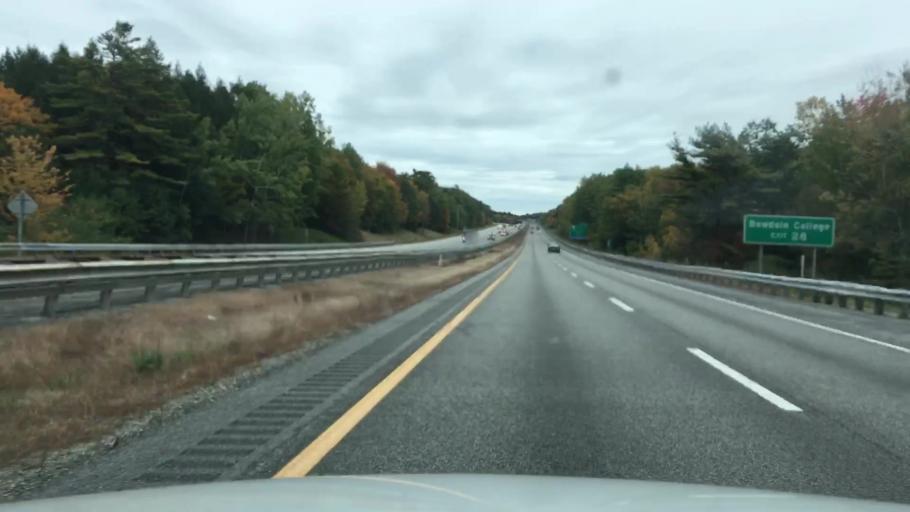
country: US
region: Maine
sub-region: Sagadahoc County
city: Topsham
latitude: 43.9094
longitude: -70.0462
